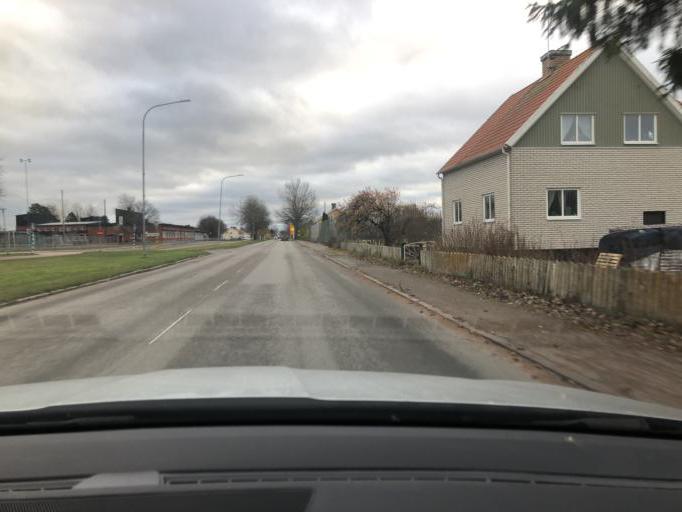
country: SE
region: Uppsala
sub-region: Tierps Kommun
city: Tierp
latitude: 60.3467
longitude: 17.5017
